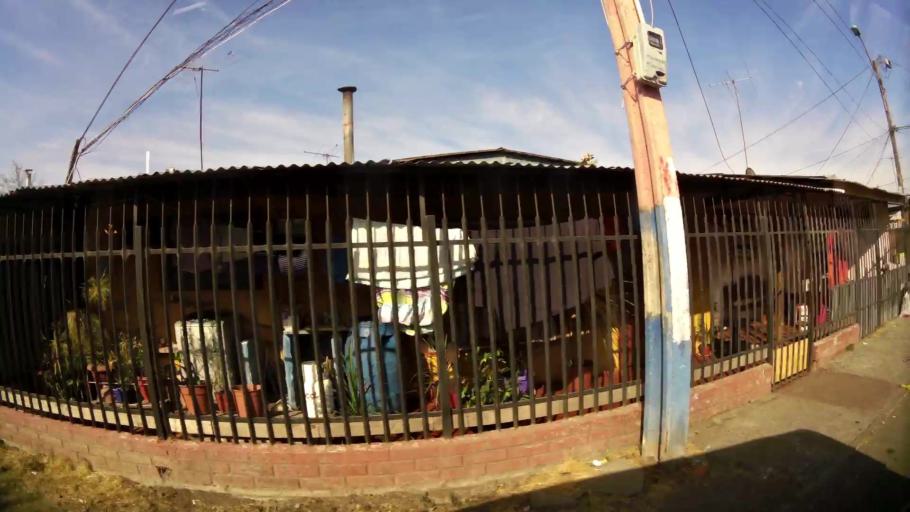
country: CL
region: Santiago Metropolitan
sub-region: Provincia de Talagante
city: Talagante
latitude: -33.6710
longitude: -70.9376
